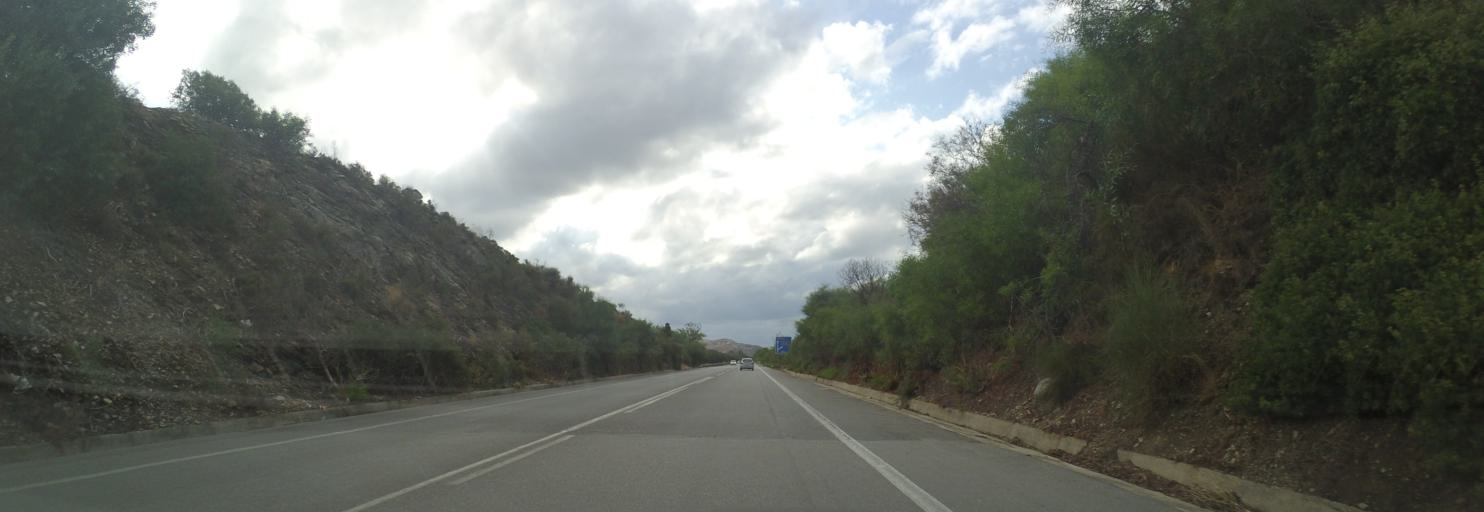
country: GR
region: Crete
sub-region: Nomos Rethymnis
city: Panormos
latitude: 35.4145
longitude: 24.7070
